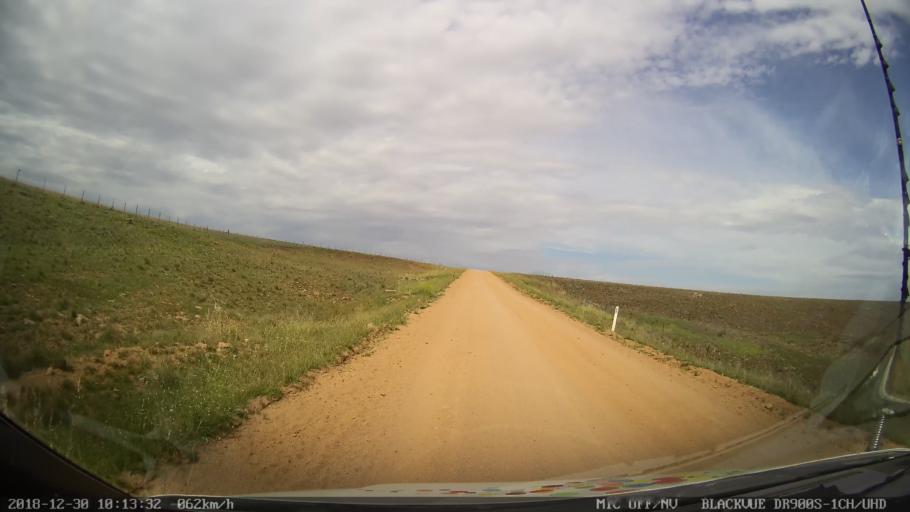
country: AU
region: New South Wales
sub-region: Snowy River
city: Berridale
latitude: -36.5381
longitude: 149.0638
